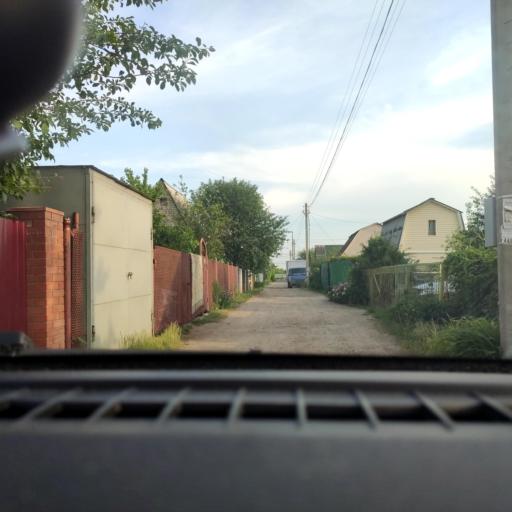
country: RU
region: Samara
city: Tol'yatti
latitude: 53.5906
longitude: 49.3233
